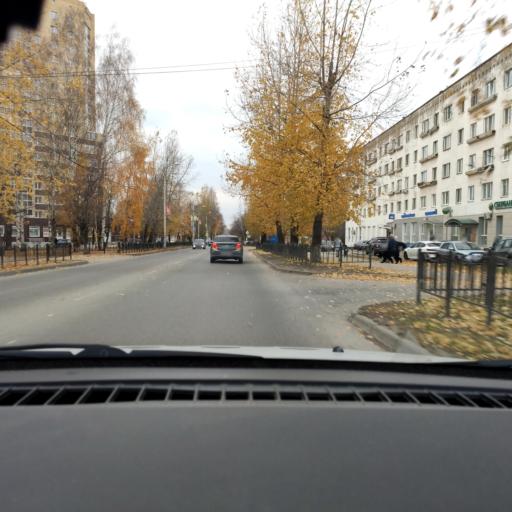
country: RU
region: Perm
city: Perm
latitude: 58.1070
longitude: 56.3810
